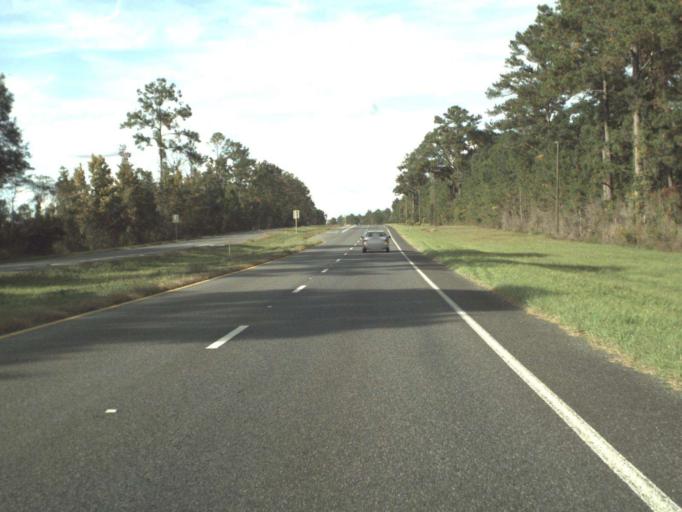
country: US
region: Florida
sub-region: Jefferson County
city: Monticello
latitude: 30.6558
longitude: -83.8770
